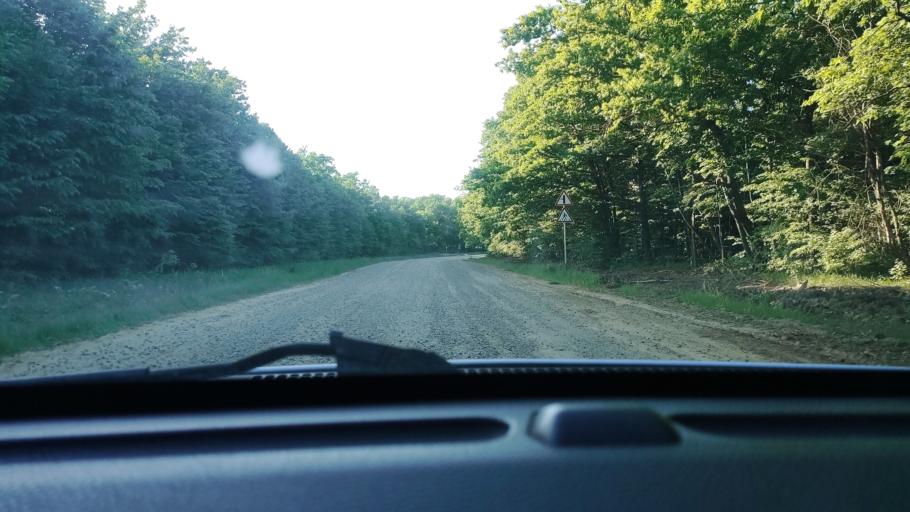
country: RU
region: Krasnodarskiy
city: Novodmitriyevskaya
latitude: 44.7196
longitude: 38.9907
